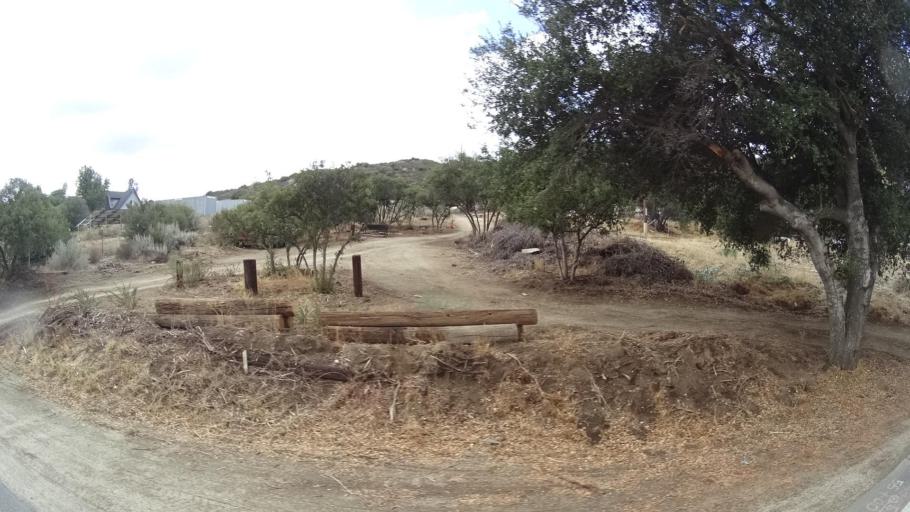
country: US
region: California
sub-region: San Diego County
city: Campo
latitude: 32.6520
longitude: -116.4875
